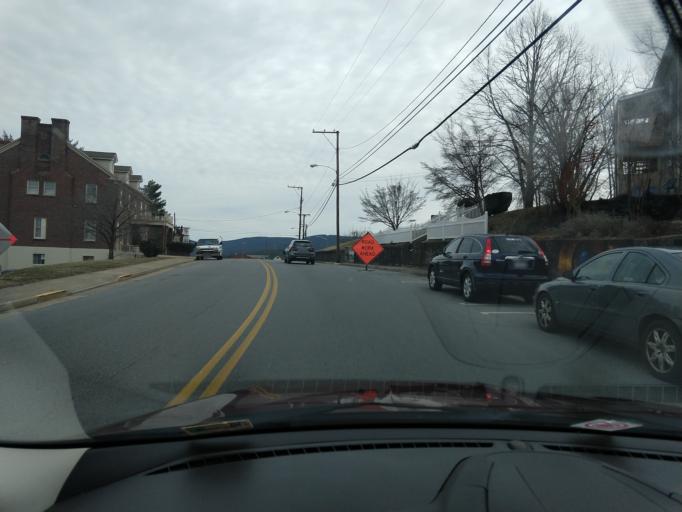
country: US
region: Virginia
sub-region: City of Waynesboro
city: Waynesboro
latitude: 38.0694
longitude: -78.8944
